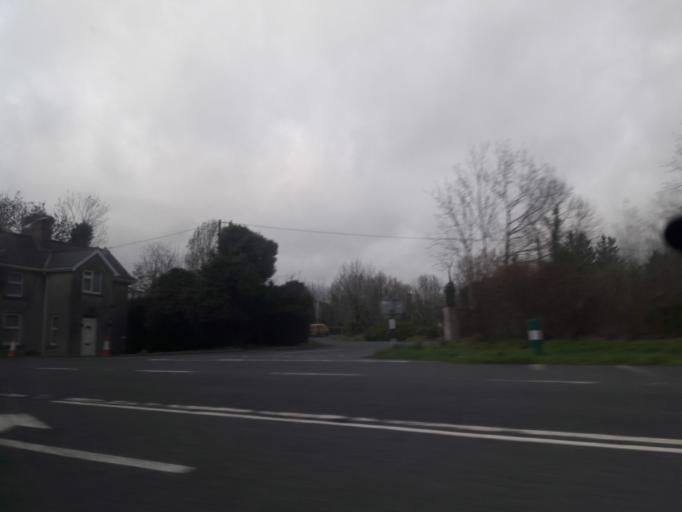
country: IE
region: Leinster
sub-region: An Longfort
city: Longford
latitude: 53.7821
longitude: -7.8365
